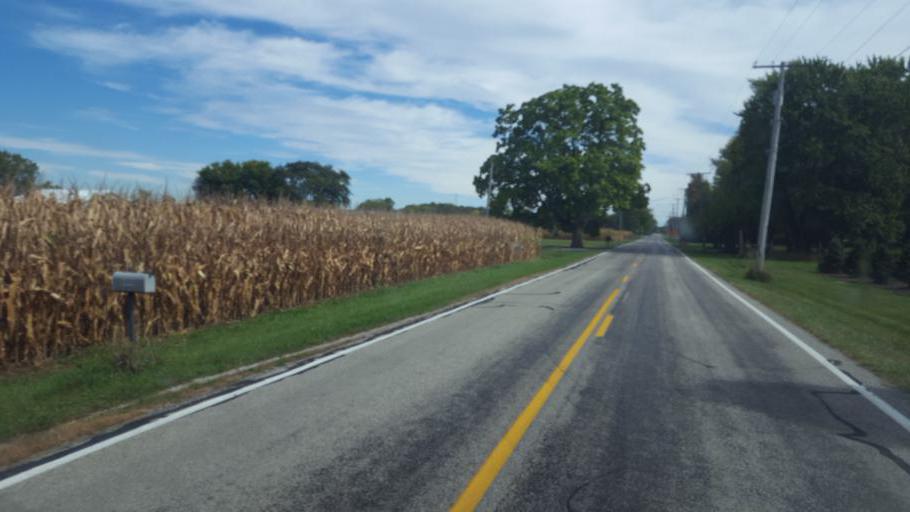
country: US
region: Ohio
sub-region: Erie County
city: Huron
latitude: 41.3649
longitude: -82.4991
